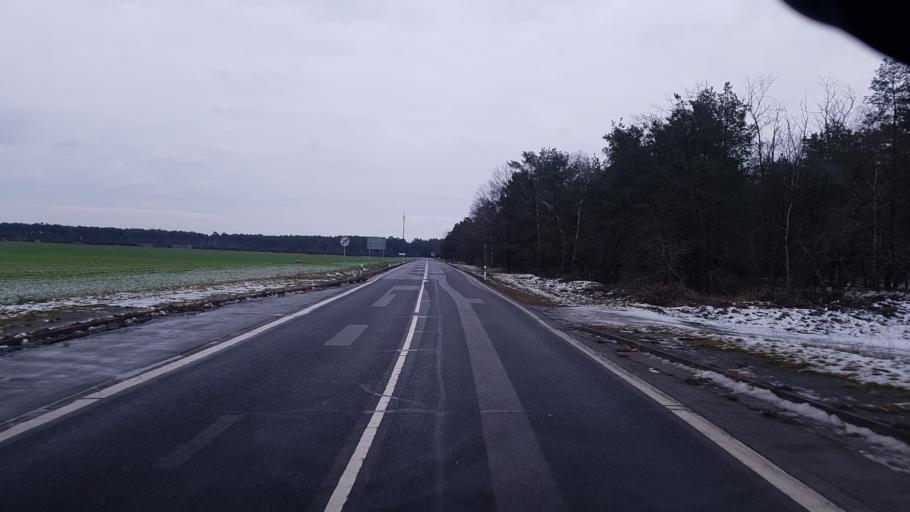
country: DE
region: Brandenburg
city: Heinersbruck
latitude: 51.8250
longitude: 14.5092
